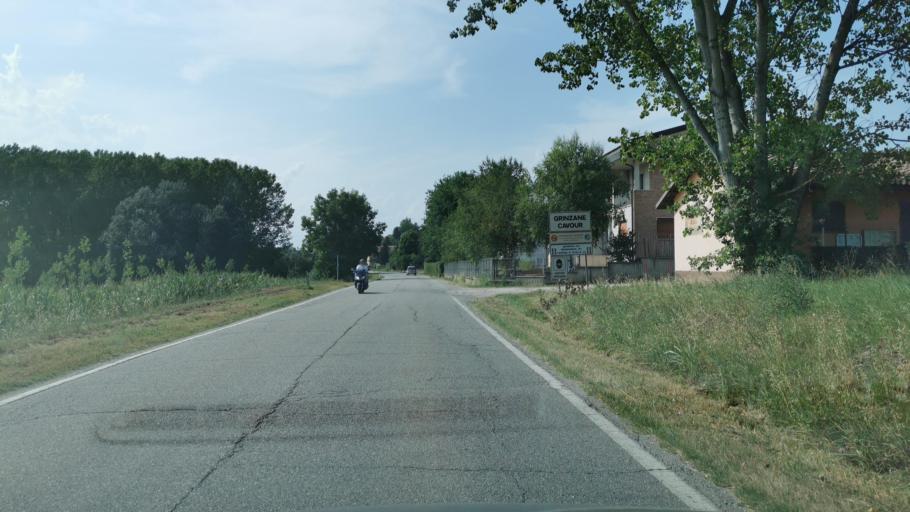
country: IT
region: Piedmont
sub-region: Provincia di Cuneo
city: Grinzane Cavour
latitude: 44.6506
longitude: 7.9920
